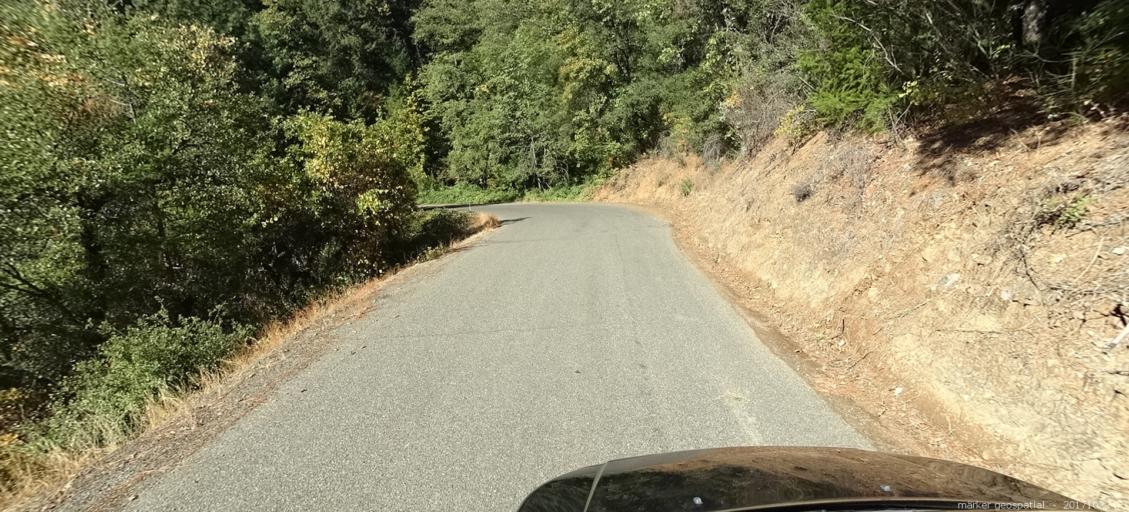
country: US
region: California
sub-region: Shasta County
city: Central Valley (historical)
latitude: 40.9329
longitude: -122.4718
